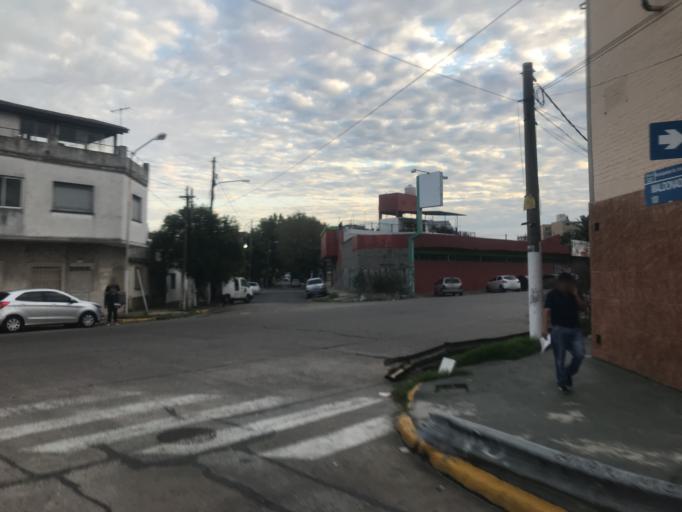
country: AR
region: Buenos Aires
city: San Justo
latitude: -34.6397
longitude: -58.5450
